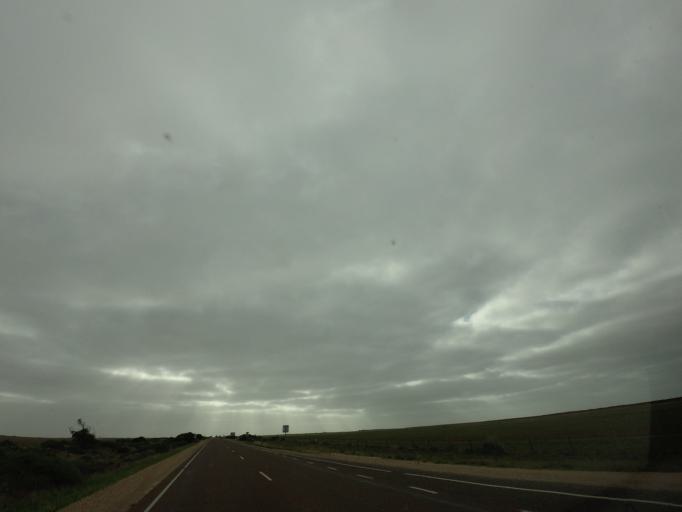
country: AU
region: South Australia
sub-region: Ceduna
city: Ceduna
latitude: -32.1237
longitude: 133.7051
